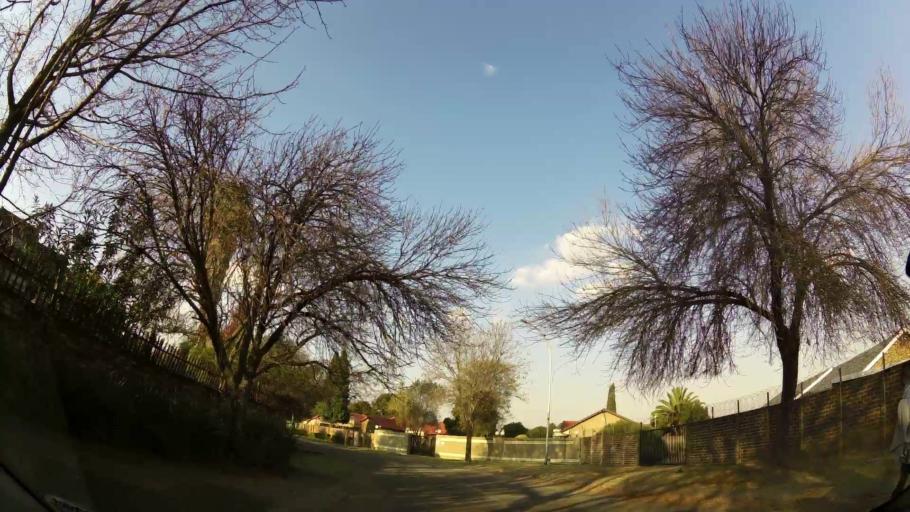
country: ZA
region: Gauteng
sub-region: Ekurhuleni Metropolitan Municipality
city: Benoni
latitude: -26.1368
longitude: 28.3747
